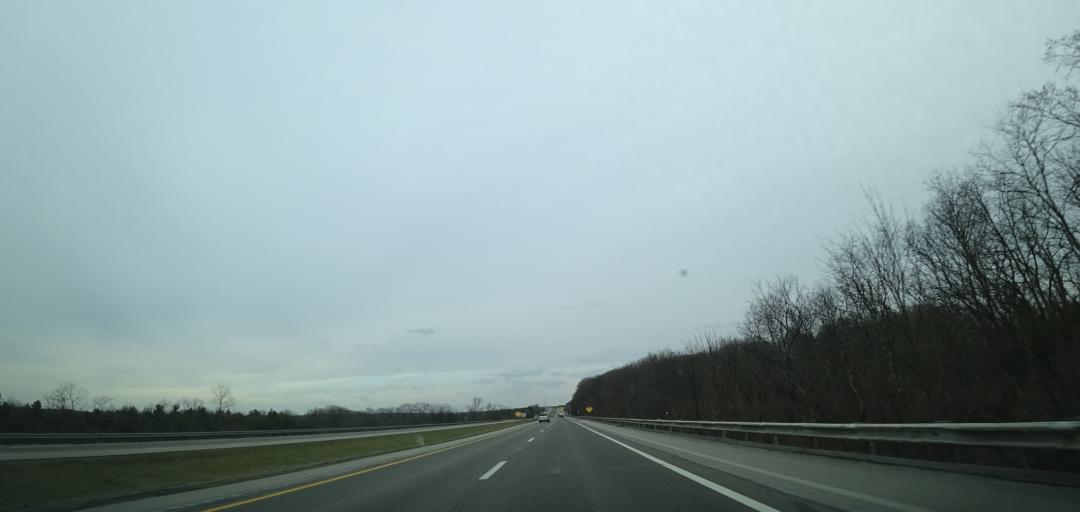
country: US
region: Ohio
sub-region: Mahoning County
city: New Middletown
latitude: 40.9345
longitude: -80.5746
